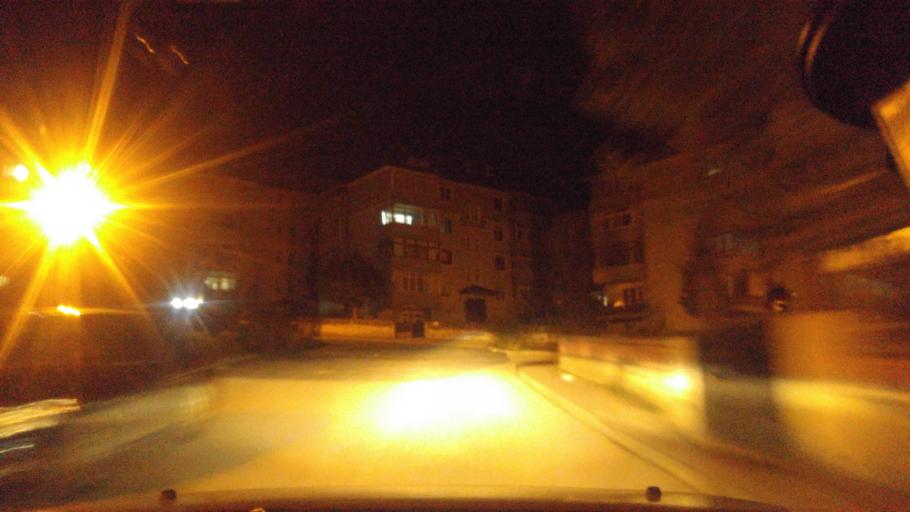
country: TR
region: Karabuk
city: Safranbolu
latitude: 41.2519
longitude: 32.6757
